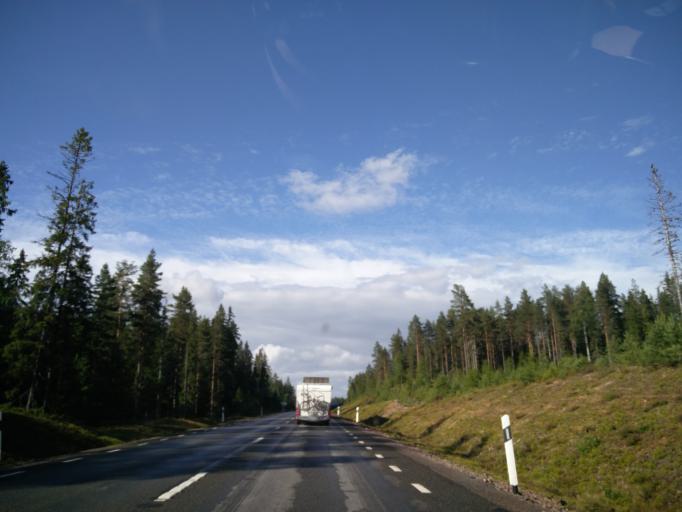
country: SE
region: Dalarna
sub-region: Malung-Saelens kommun
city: Malung
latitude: 60.5079
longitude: 13.4321
